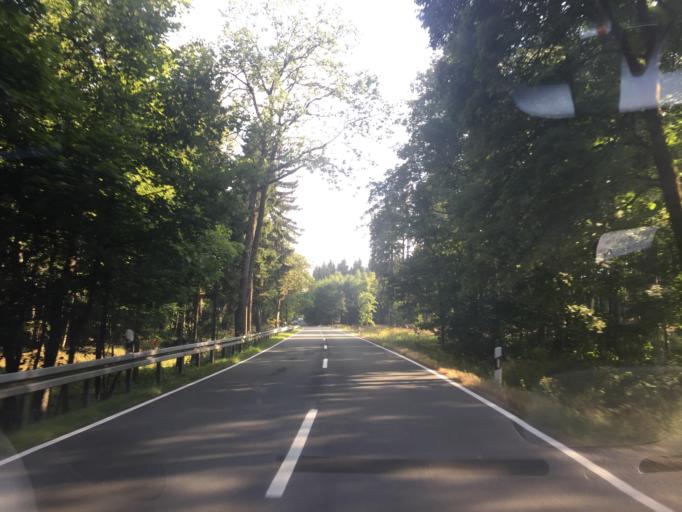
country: DE
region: Saxony-Anhalt
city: Darlingerode
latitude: 51.7760
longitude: 10.7306
